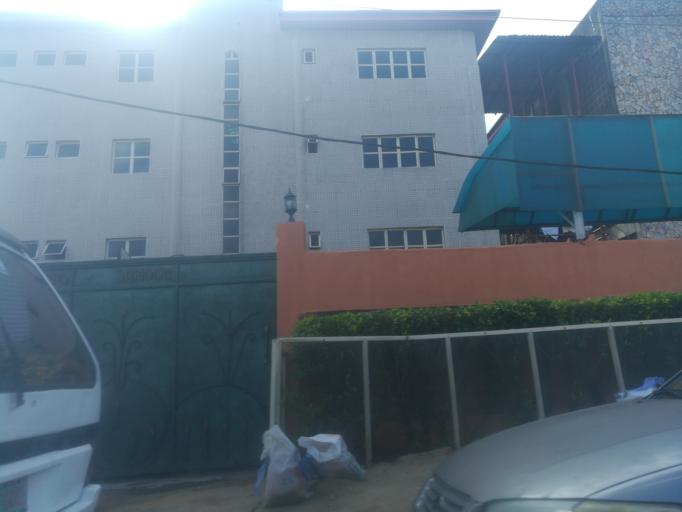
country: NG
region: Lagos
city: Somolu
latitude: 6.5416
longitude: 3.3756
